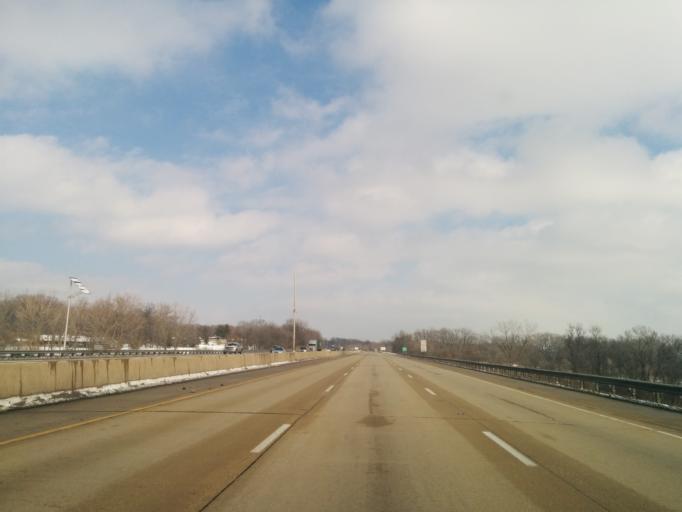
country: US
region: Illinois
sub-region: Will County
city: Mokena
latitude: 41.5449
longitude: -87.9317
